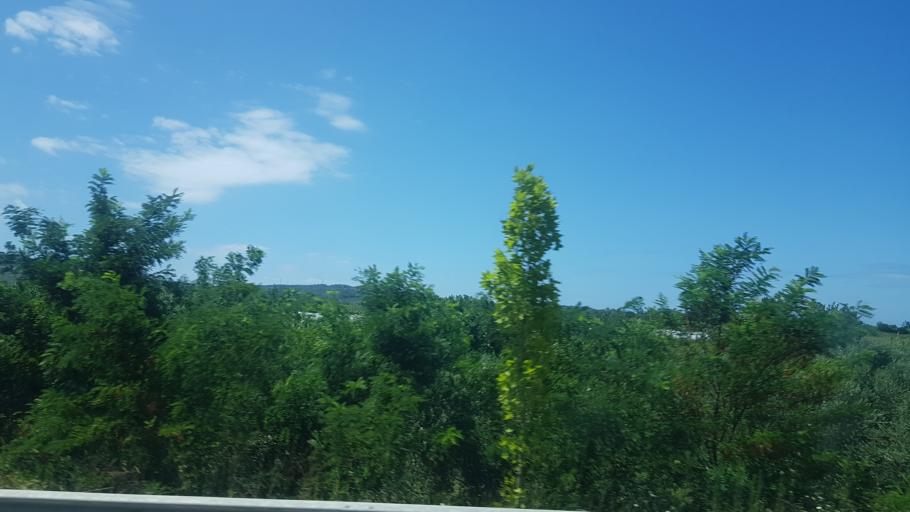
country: AL
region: Fier
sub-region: Rrethi i Fierit
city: Frakulla e Madhe
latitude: 40.6155
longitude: 19.5212
